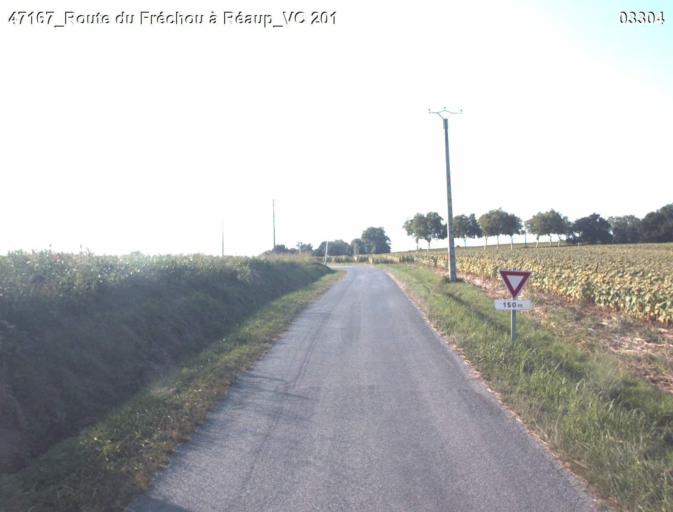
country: FR
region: Aquitaine
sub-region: Departement du Lot-et-Garonne
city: Mezin
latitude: 44.0703
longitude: 0.2762
